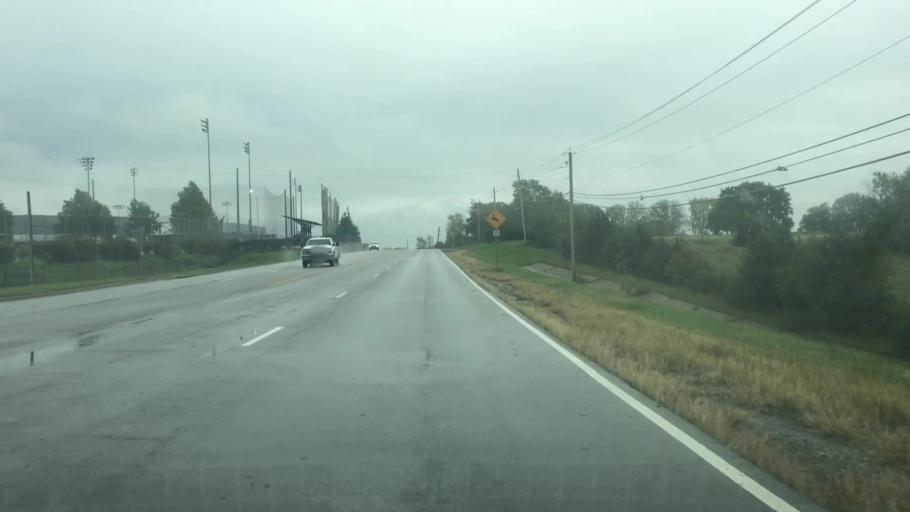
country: US
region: Kansas
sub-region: Johnson County
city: Lenexa
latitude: 38.9709
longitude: -94.8017
